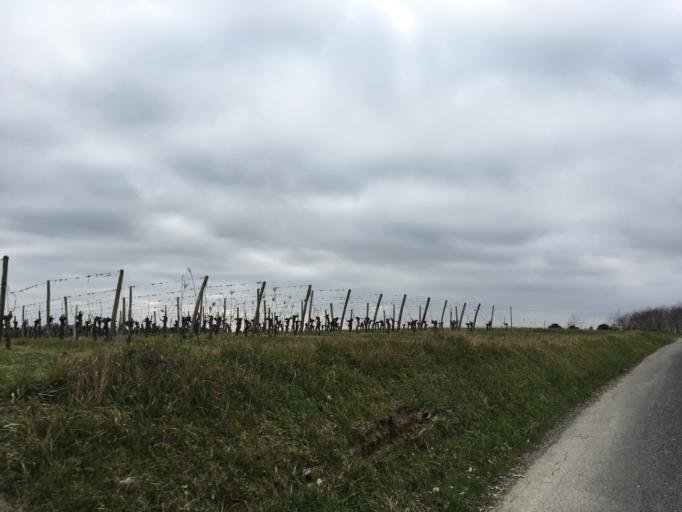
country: FR
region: Aquitaine
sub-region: Departement de la Gironde
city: Saint-Ciers-sur-Gironde
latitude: 45.3178
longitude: -0.5844
